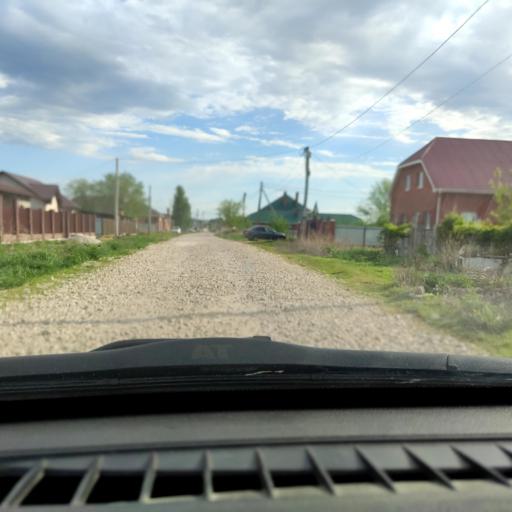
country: RU
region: Samara
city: Tol'yatti
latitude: 53.5680
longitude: 49.4082
